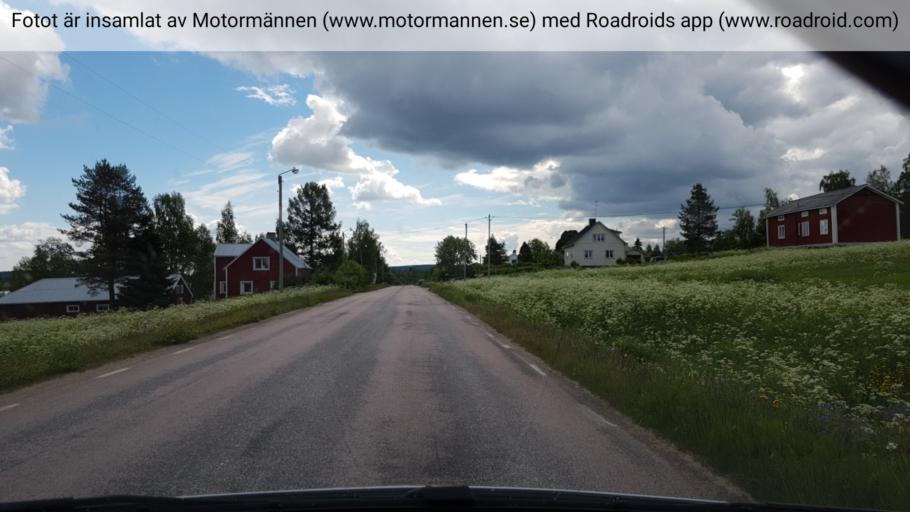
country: FI
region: Lapland
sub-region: Torniolaakso
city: Ylitornio
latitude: 66.2268
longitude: 23.6889
